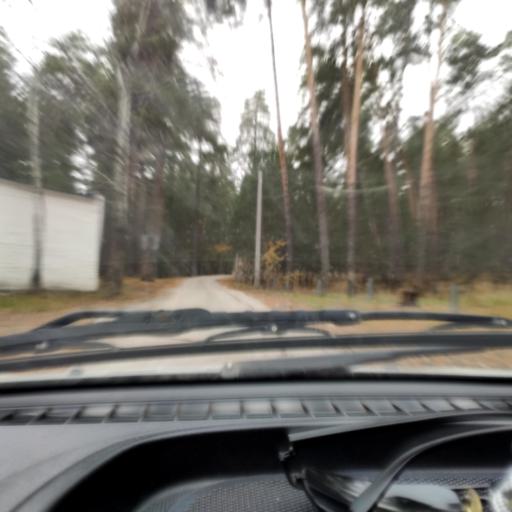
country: RU
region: Samara
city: Tol'yatti
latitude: 53.4744
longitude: 49.3340
